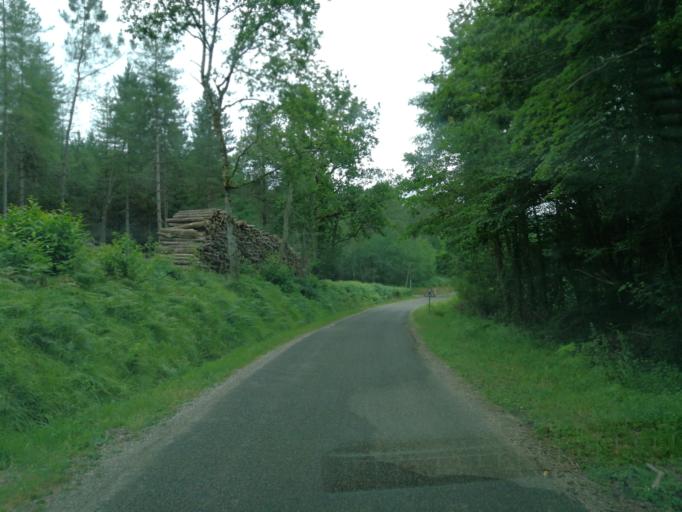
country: FR
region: Aquitaine
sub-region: Departement du Lot-et-Garonne
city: Montayral
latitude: 44.5586
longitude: 1.0743
